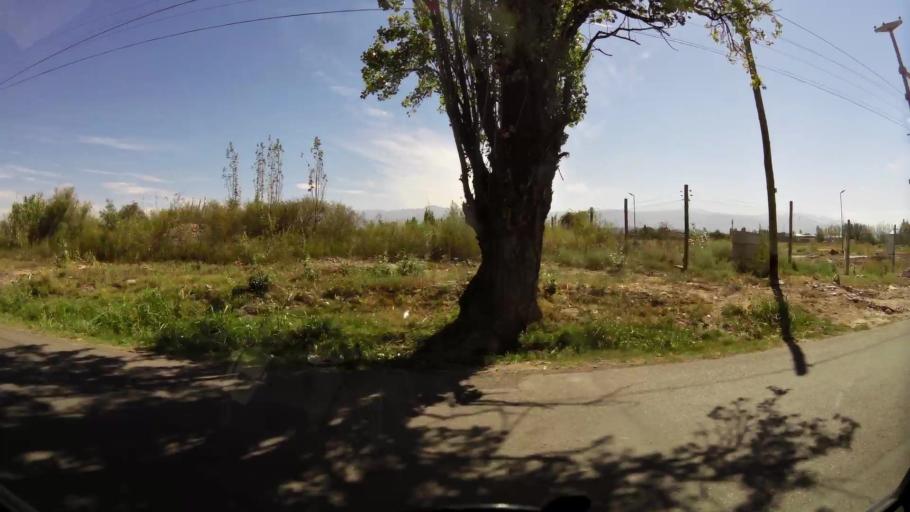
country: AR
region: Mendoza
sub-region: Departamento de Godoy Cruz
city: Godoy Cruz
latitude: -32.9824
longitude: -68.8431
